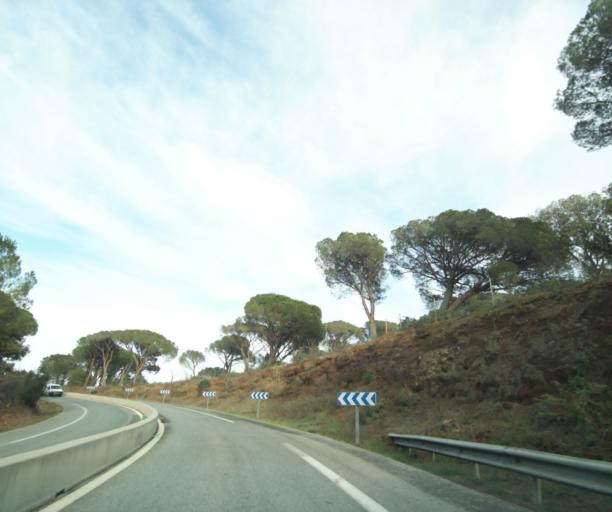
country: FR
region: Provence-Alpes-Cote d'Azur
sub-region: Departement du Var
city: Le Muy
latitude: 43.4575
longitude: 6.5532
